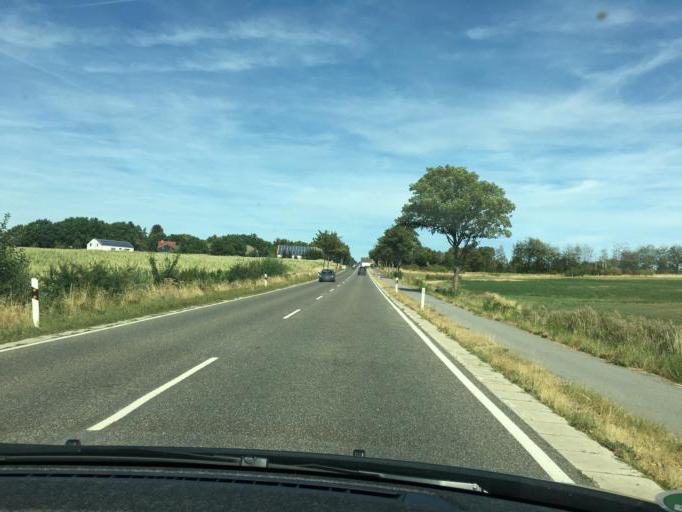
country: DE
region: North Rhine-Westphalia
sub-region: Regierungsbezirk Koln
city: Hurtgenwald
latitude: 50.7179
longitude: 6.3889
